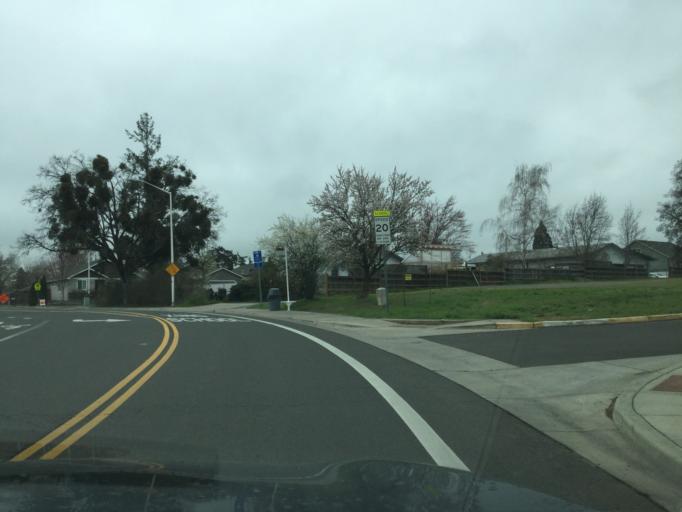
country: US
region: Oregon
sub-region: Jackson County
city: Central Point
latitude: 42.3867
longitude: -122.9195
